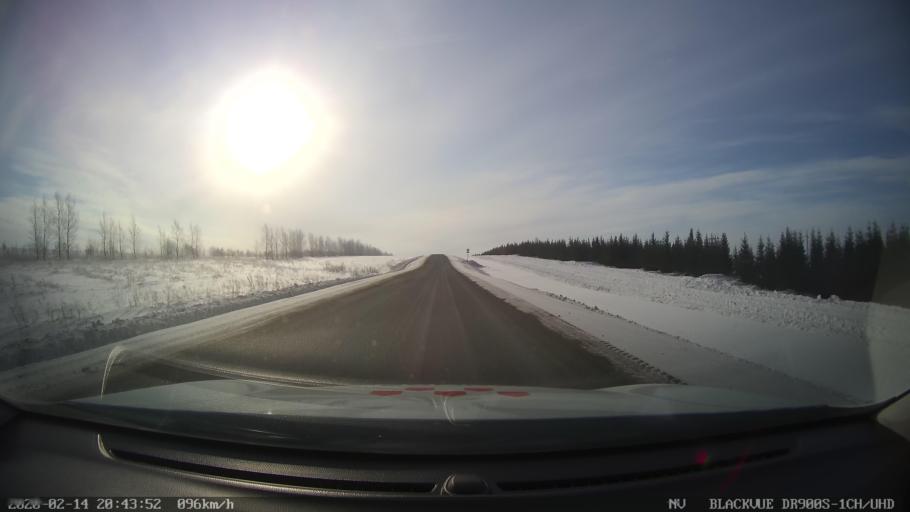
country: RU
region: Tatarstan
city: Kuybyshevskiy Zaton
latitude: 55.3022
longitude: 49.1477
